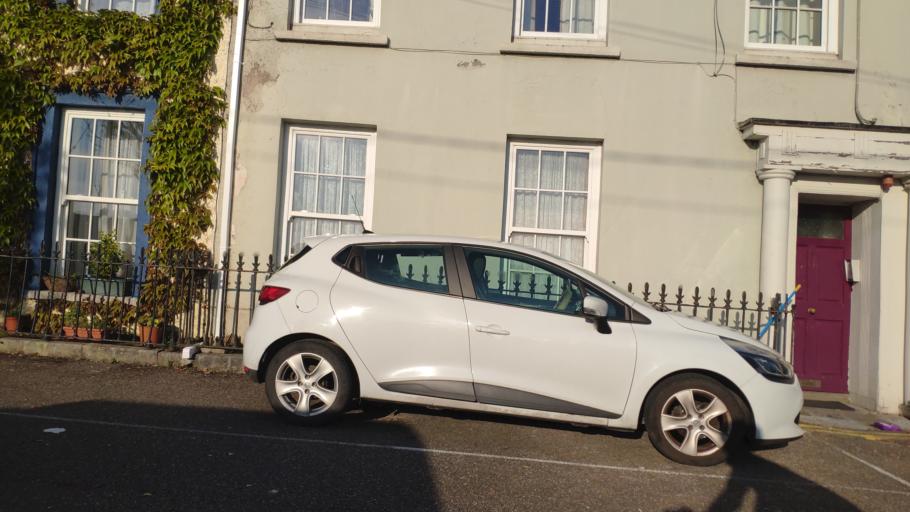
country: IE
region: Munster
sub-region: County Cork
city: Cork
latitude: 51.9050
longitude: -8.4699
